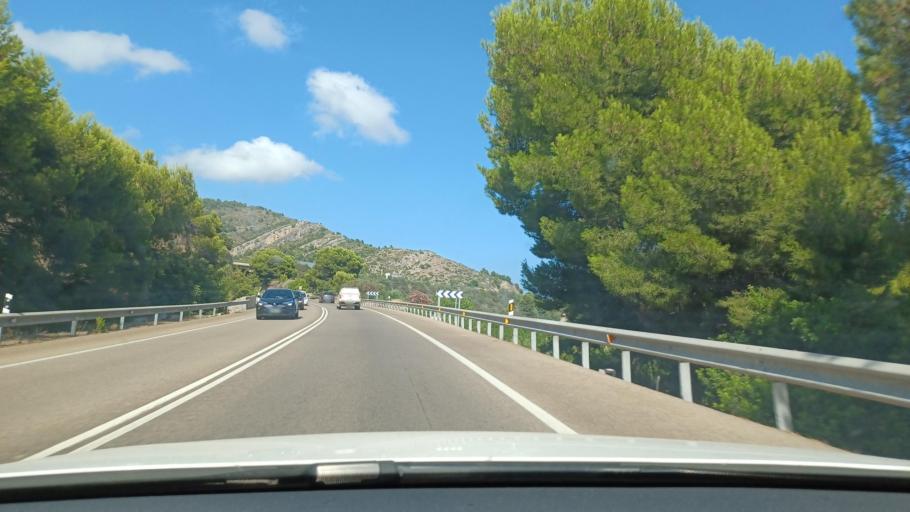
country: ES
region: Valencia
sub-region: Provincia de Castello
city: Benicassim
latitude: 40.0648
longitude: 0.0798
